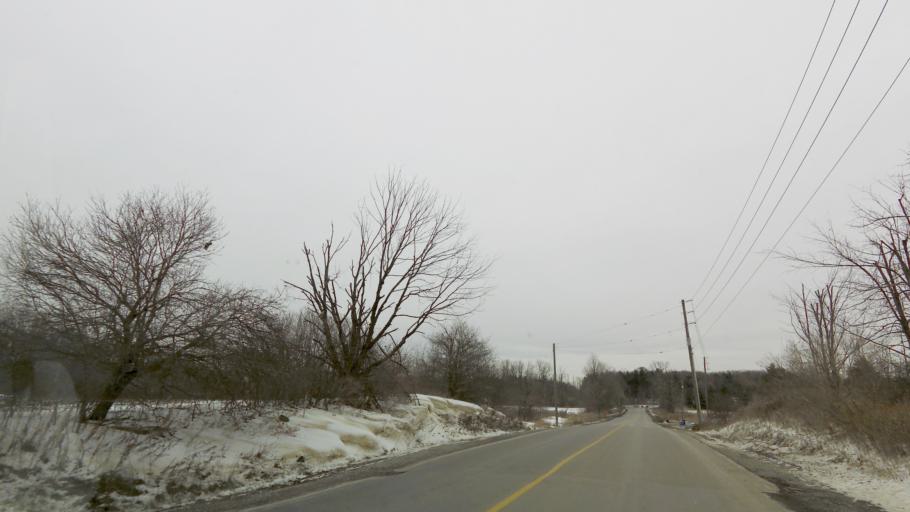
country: CA
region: Ontario
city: Vaughan
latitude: 43.8750
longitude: -79.5988
